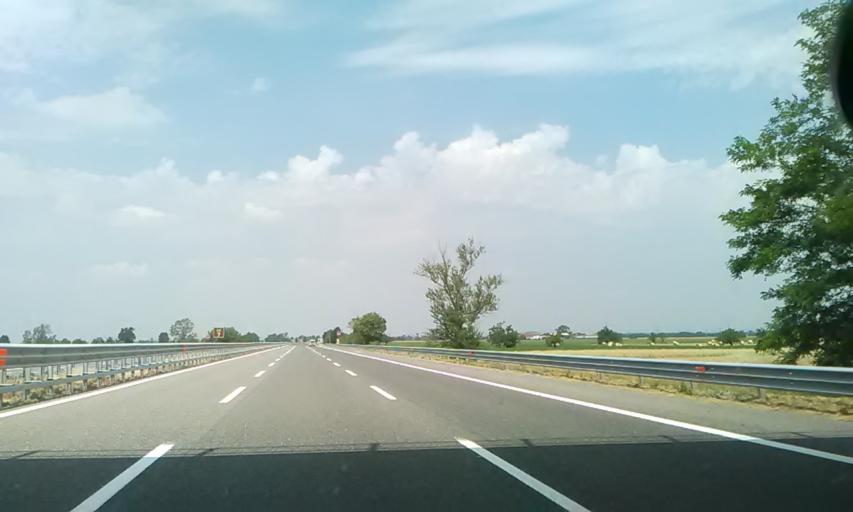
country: IT
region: Piedmont
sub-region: Provincia di Alessandria
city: Castelspina
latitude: 44.8043
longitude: 8.6032
